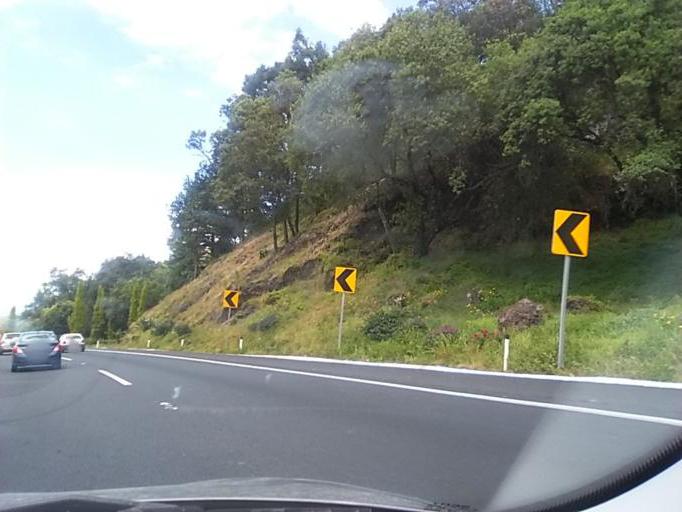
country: MX
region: Morelos
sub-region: Tepoztlan
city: Santa Catarina
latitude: 19.0204
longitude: -99.1407
